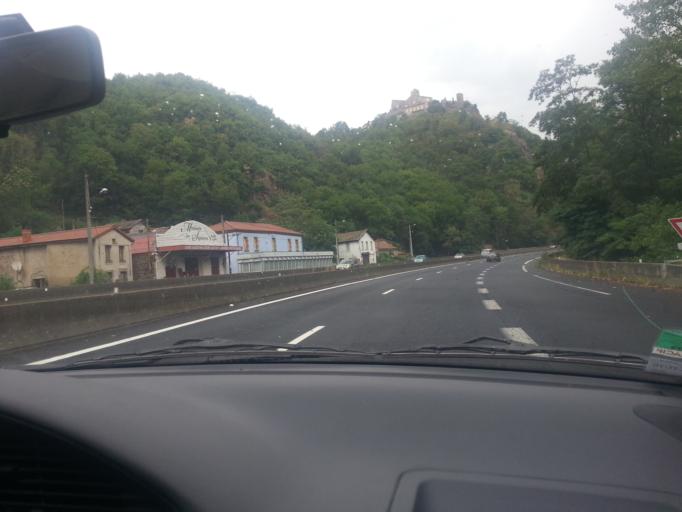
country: FR
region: Auvergne
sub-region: Departement du Puy-de-Dome
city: Issoire
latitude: 45.5816
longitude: 3.2405
